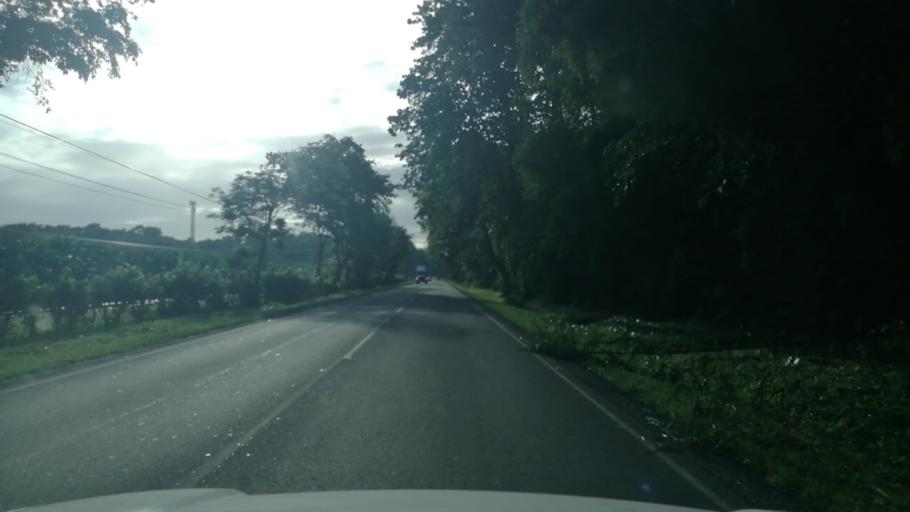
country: CR
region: Limon
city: Matina
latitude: 10.0375
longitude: -83.2698
